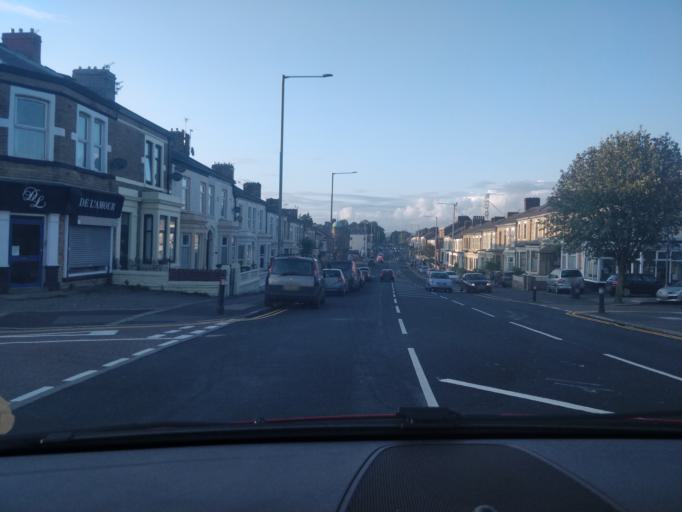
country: GB
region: England
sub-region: Lancashire
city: Preston
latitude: 53.7670
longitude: -2.6918
